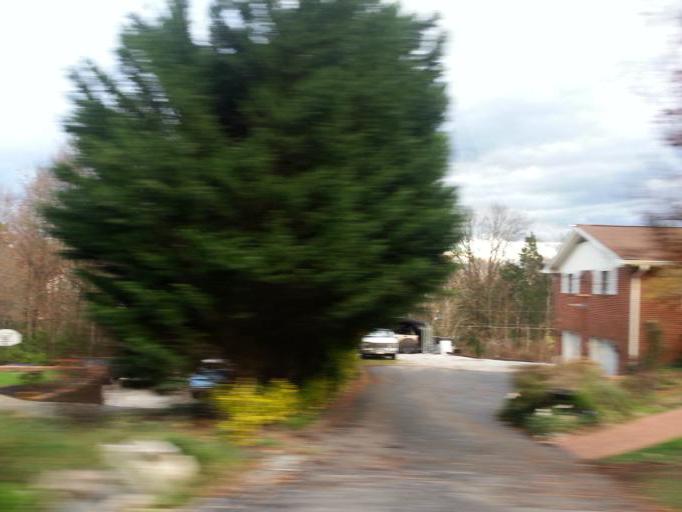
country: US
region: Tennessee
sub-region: Knox County
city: Knoxville
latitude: 35.9290
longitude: -84.0159
